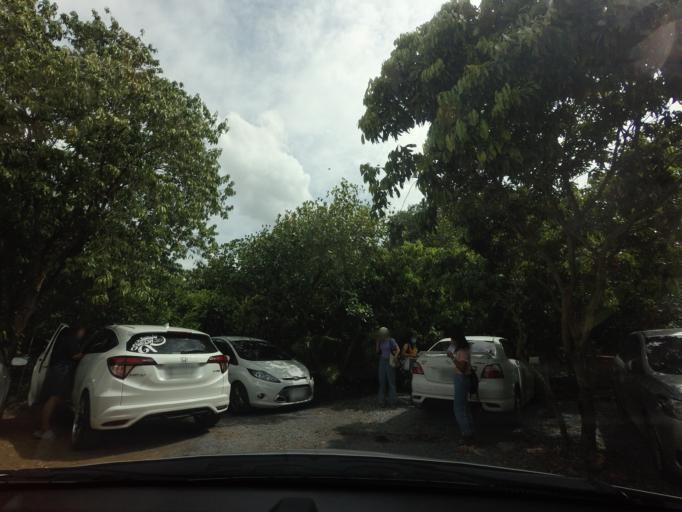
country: TH
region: Bangkok
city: Chom Thong
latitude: 13.6912
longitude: 100.4667
